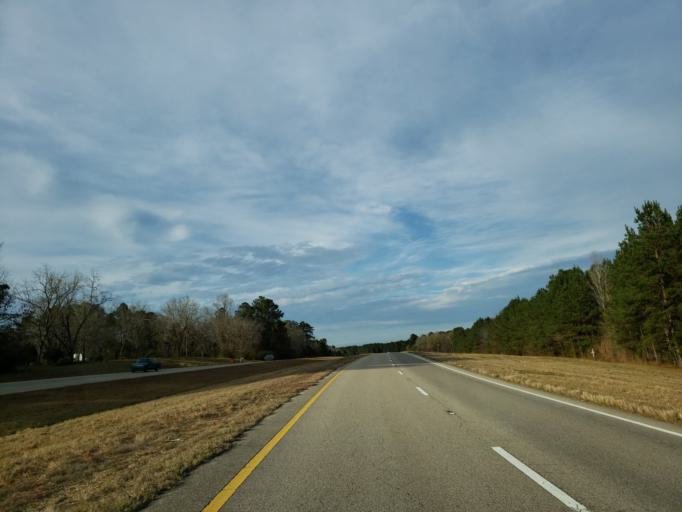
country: US
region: Mississippi
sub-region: Wayne County
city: Waynesboro
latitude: 31.8059
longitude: -88.6909
